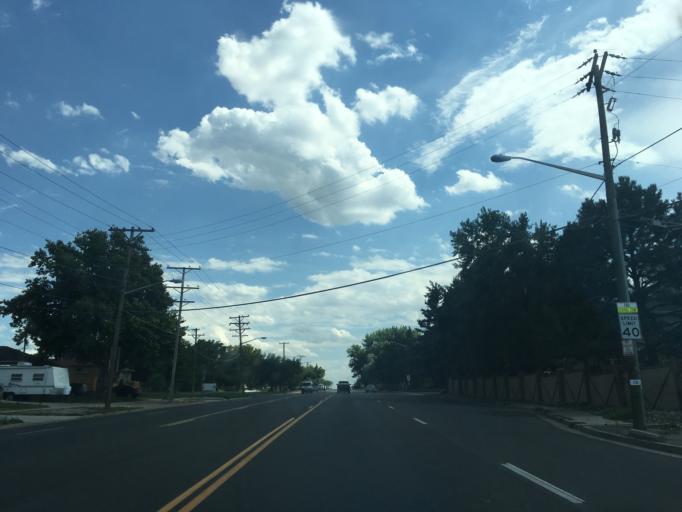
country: US
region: Colorado
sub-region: Arapahoe County
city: Sheridan
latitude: 39.6755
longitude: -105.0533
